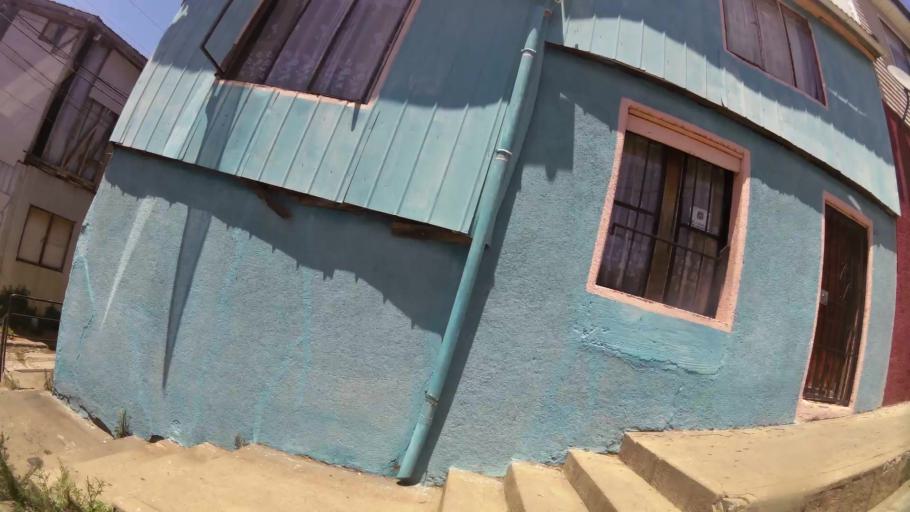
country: CL
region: Valparaiso
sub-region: Provincia de Valparaiso
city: Valparaiso
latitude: -33.0356
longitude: -71.6379
